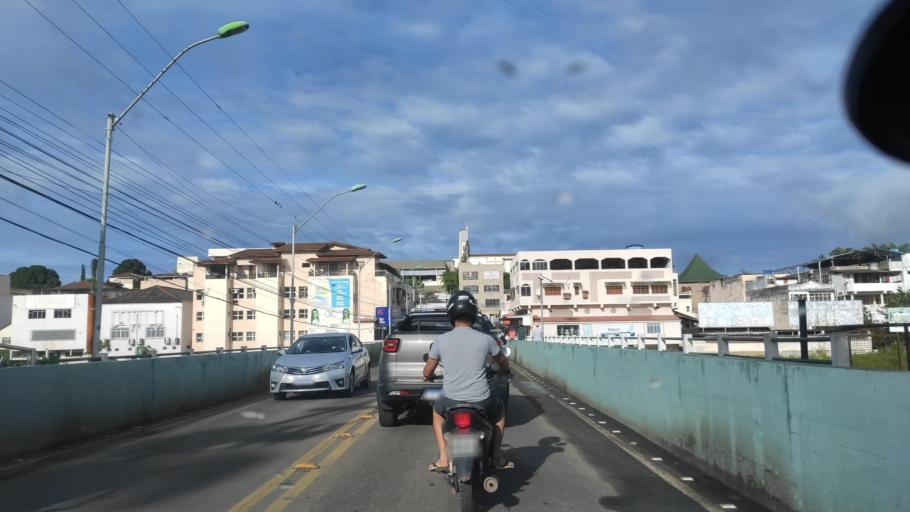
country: BR
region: Espirito Santo
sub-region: Nova Venecia
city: Nova Venecia
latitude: -18.7090
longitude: -40.3987
